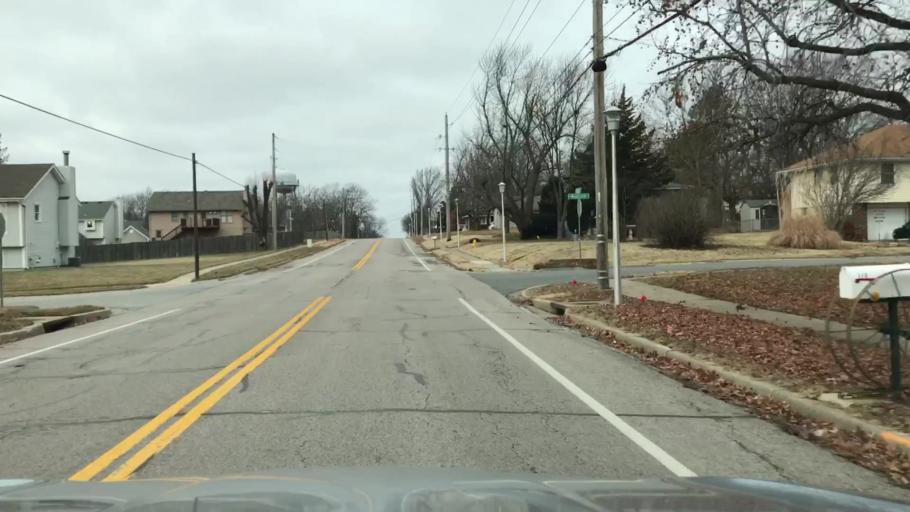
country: US
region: Missouri
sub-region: Jackson County
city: Lees Summit
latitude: 38.8964
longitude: -94.3835
